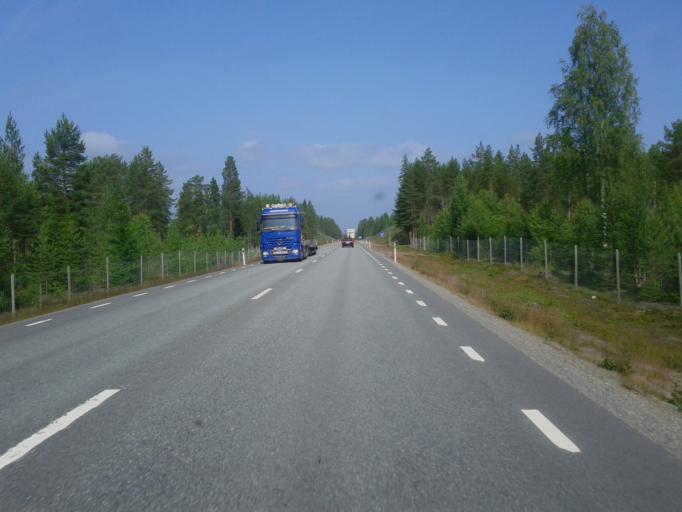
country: SE
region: Vaesterbotten
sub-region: Skelleftea Kommun
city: Burea
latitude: 64.5909
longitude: 21.2135
